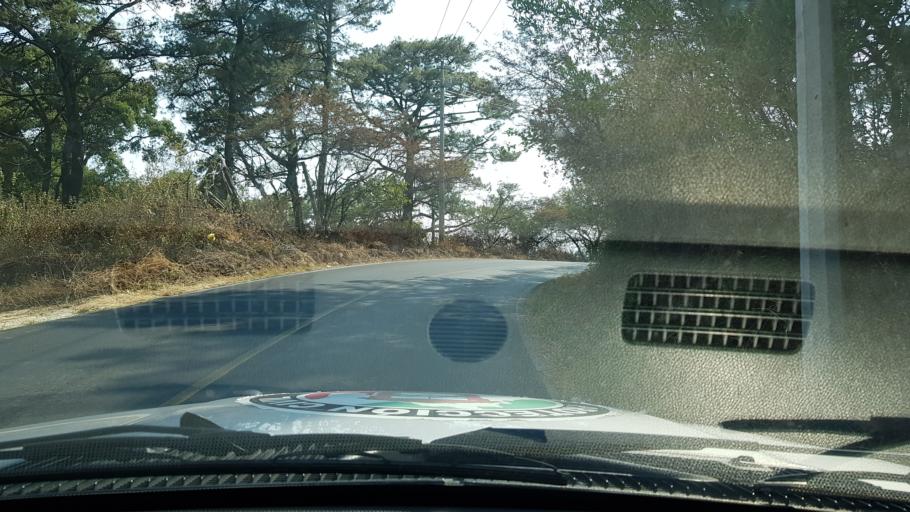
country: MX
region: Mexico
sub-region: Ozumba
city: San Jose Tlacotitlan
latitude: 18.9896
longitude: -98.8198
